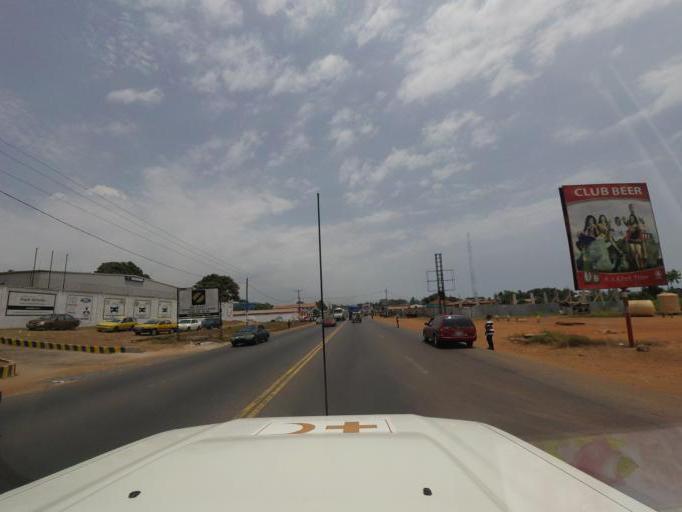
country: LR
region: Montserrado
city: Monrovia
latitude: 6.2751
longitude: -10.7505
